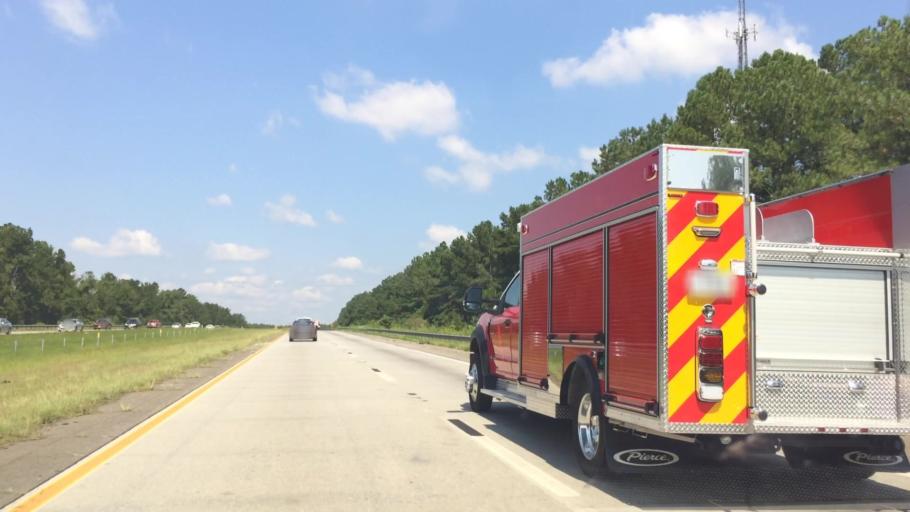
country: US
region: South Carolina
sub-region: Colleton County
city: Walterboro
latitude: 33.0327
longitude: -80.6675
